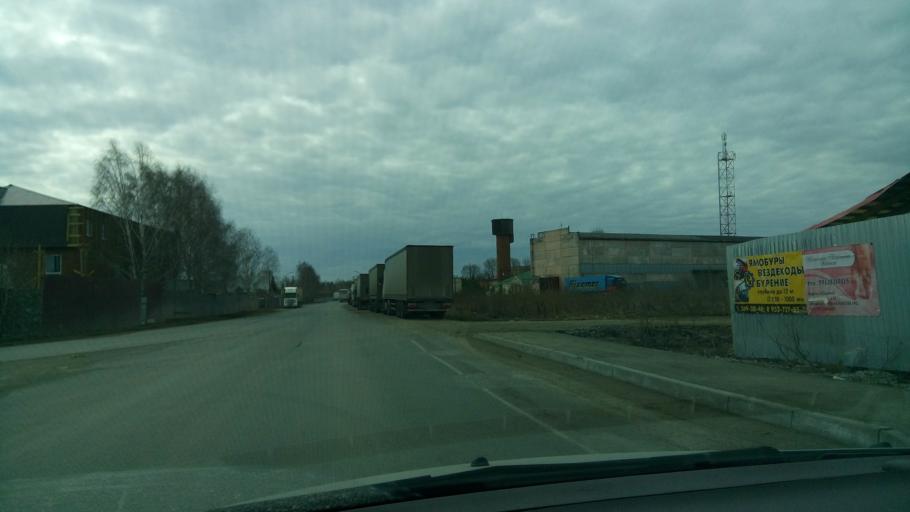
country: RU
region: Sverdlovsk
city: Verkhnyaya Pyshma
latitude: 56.9580
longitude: 60.6692
